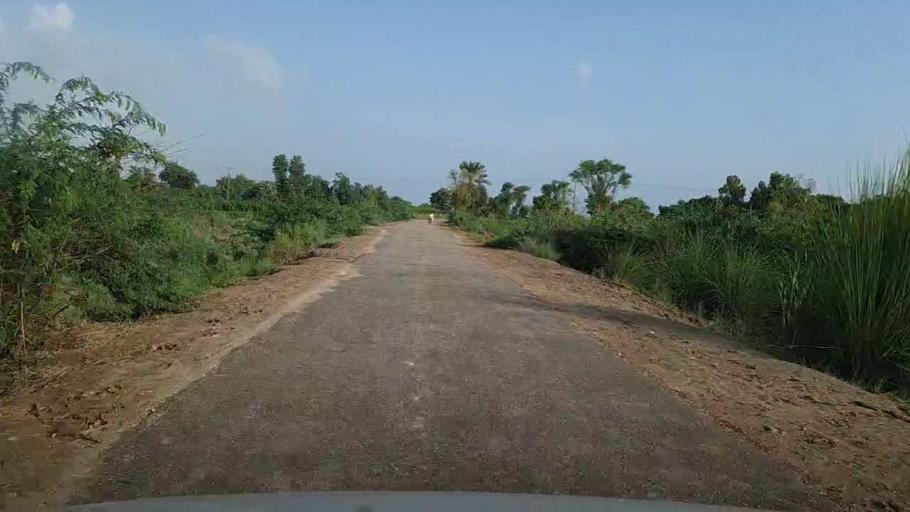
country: PK
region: Sindh
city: Pad Idan
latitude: 26.8021
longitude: 68.2356
